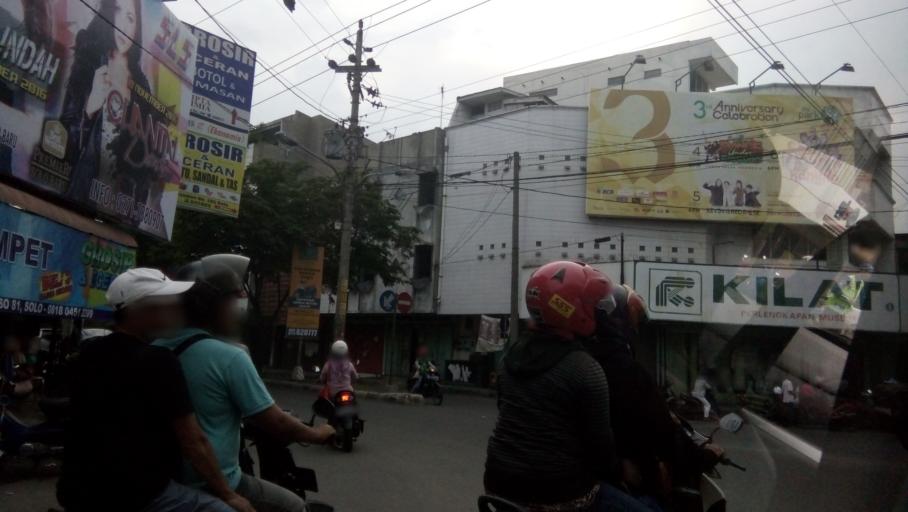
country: ID
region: Central Java
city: Surakarta
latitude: -7.5744
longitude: 110.8233
